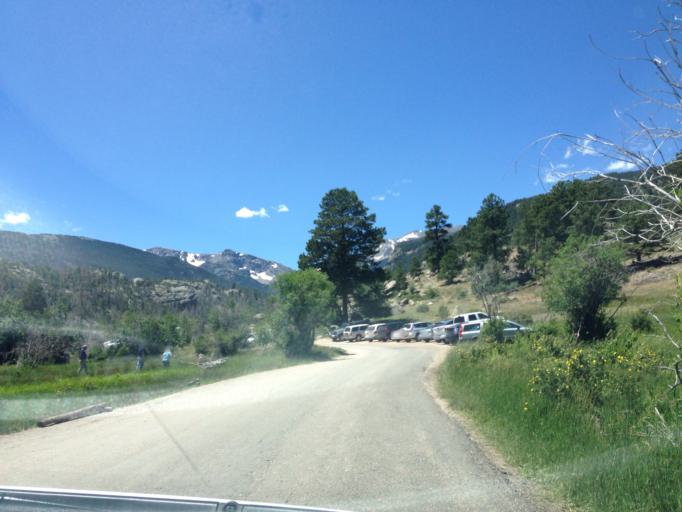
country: US
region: Colorado
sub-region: Larimer County
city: Estes Park
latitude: 40.3567
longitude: -105.6144
